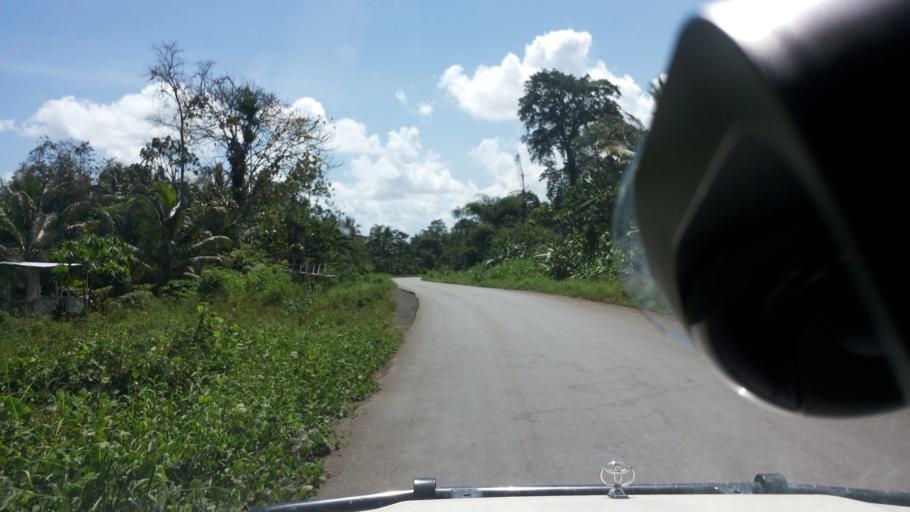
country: PG
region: Madang
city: Madang
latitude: -5.5340
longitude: 145.3855
